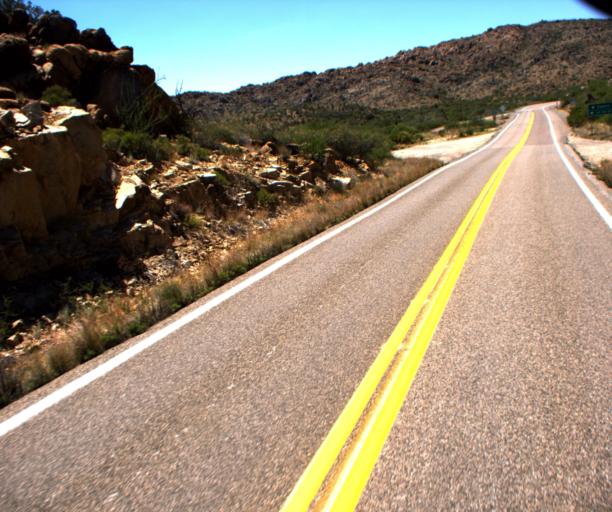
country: US
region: Arizona
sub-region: Yavapai County
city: Bagdad
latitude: 34.5261
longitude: -113.1309
